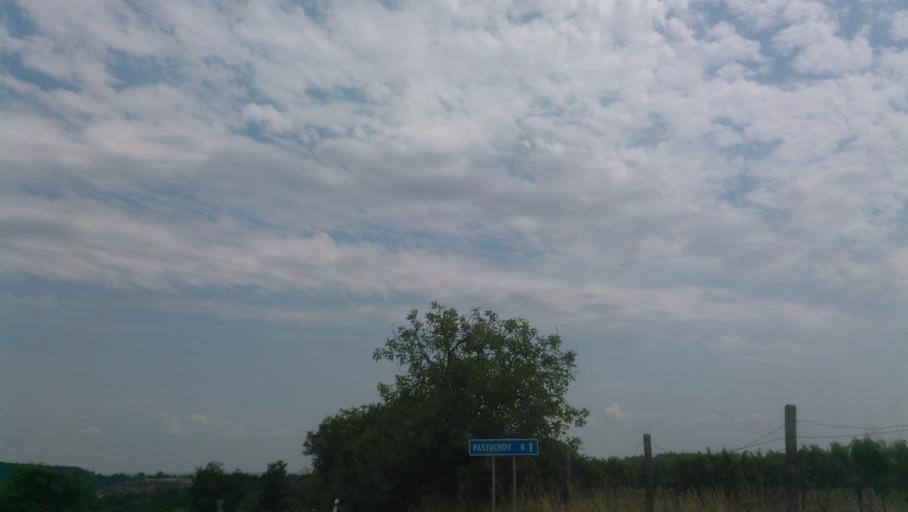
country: SK
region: Trnavsky
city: Hlohovec
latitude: 48.4378
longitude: 17.8378
